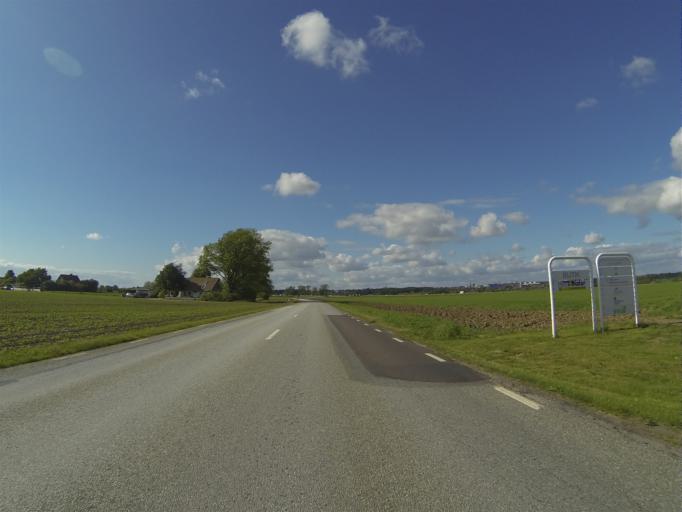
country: SE
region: Skane
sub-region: Staffanstorps Kommun
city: Staffanstorp
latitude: 55.6706
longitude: 13.1869
